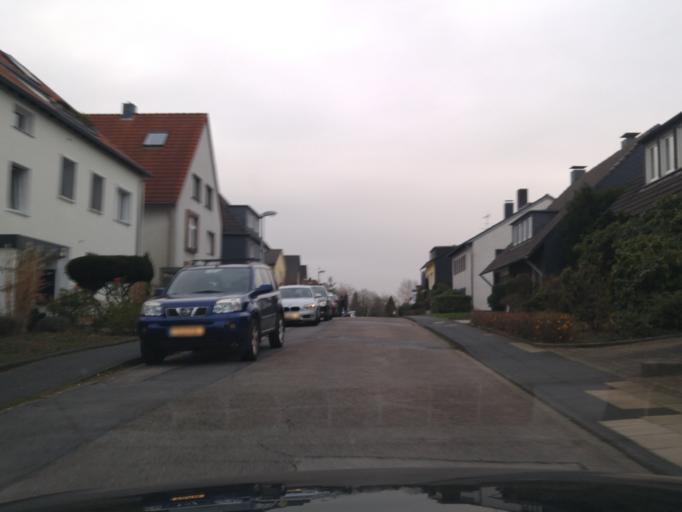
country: DE
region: North Rhine-Westphalia
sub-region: Regierungsbezirk Dusseldorf
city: Velbert
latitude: 51.4042
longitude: 7.0608
